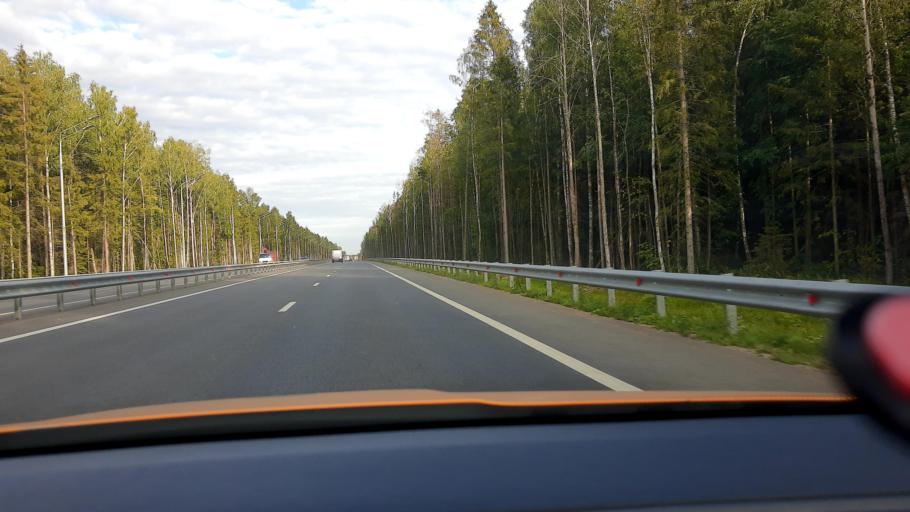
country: RU
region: Moskovskaya
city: Zvenigorod
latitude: 55.6729
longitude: 36.9101
